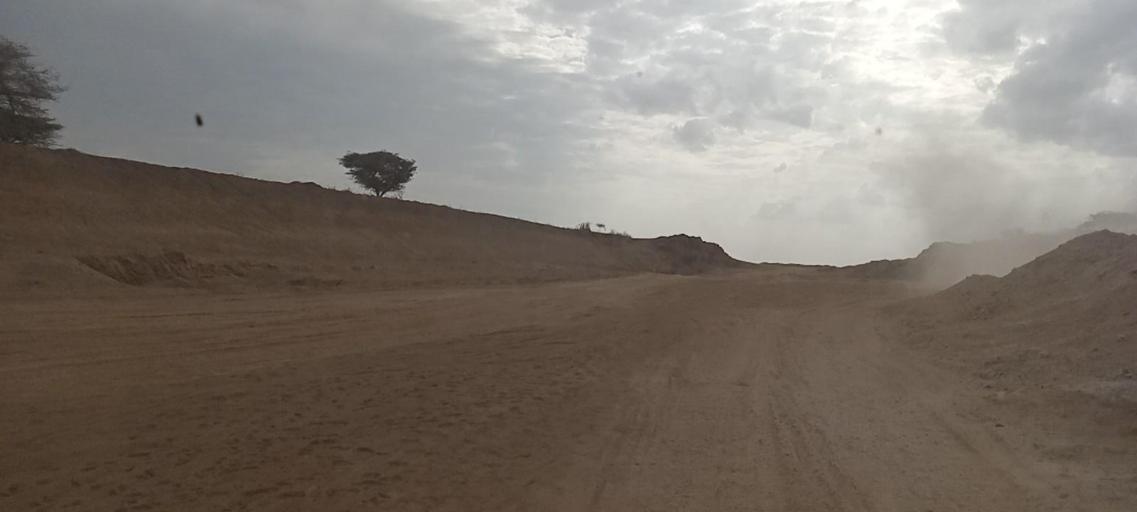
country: ET
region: Oromiya
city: Ziway
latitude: 7.7943
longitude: 38.6280
